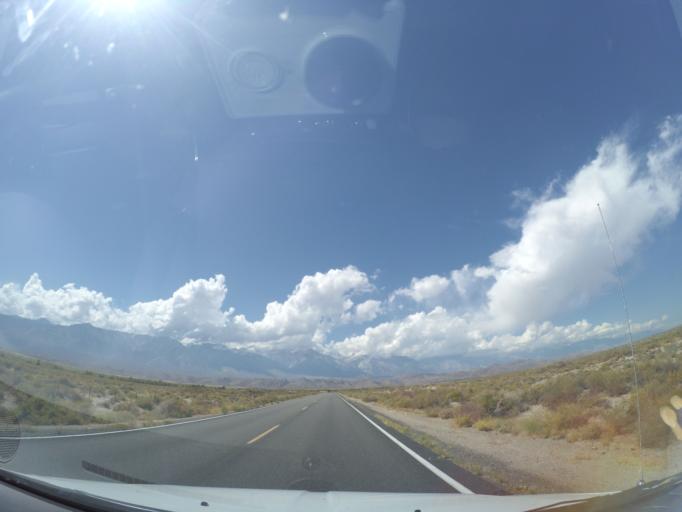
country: US
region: California
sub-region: Inyo County
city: Lone Pine
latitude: 36.5743
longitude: -118.0027
